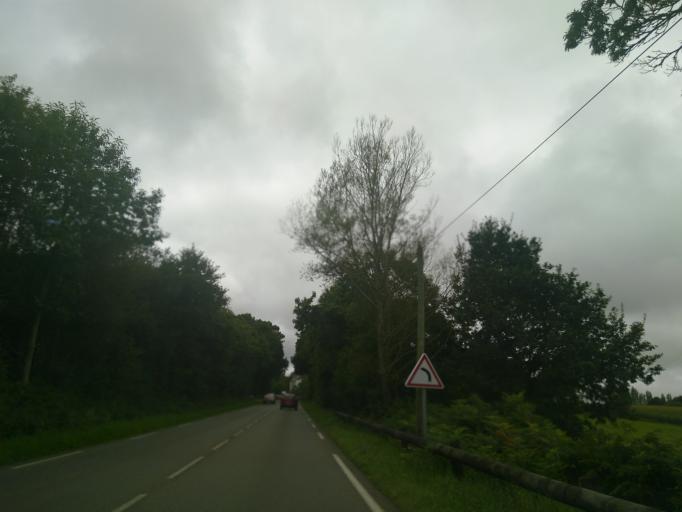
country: FR
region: Brittany
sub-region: Departement du Finistere
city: Poullan-sur-Mer
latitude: 48.0576
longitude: -4.3794
